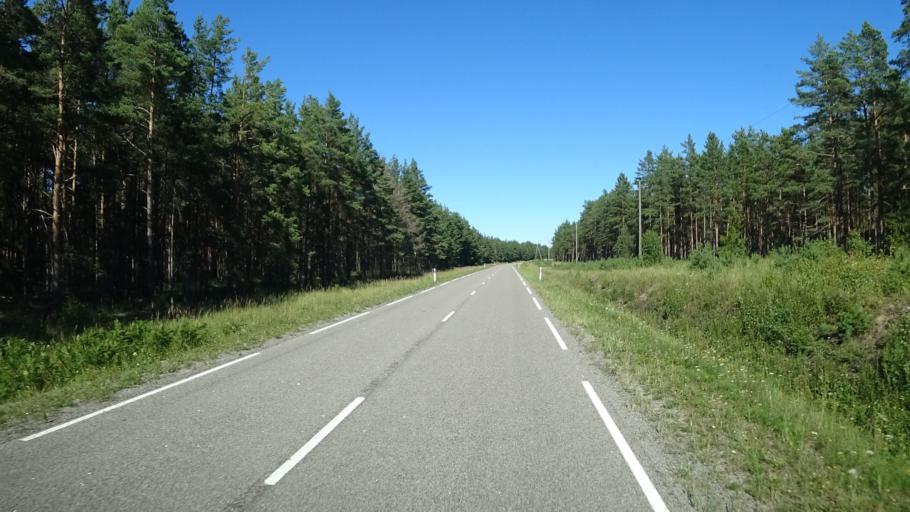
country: LV
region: Dundaga
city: Dundaga
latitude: 57.6780
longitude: 22.3478
